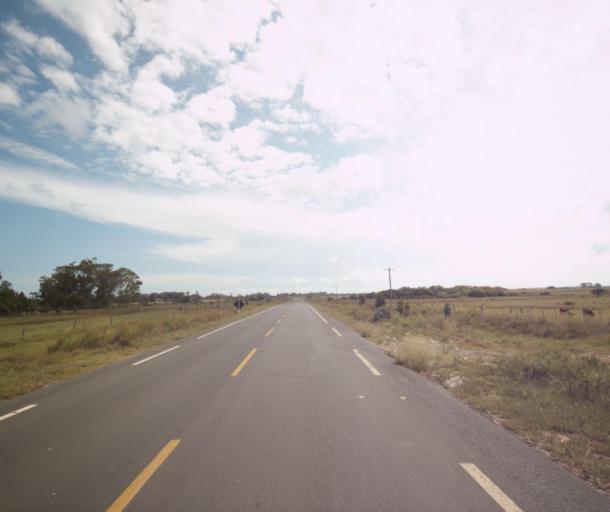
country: BR
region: Rio Grande do Sul
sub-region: Sao Lourenco Do Sul
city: Sao Lourenco do Sul
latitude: -31.6090
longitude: -51.3912
